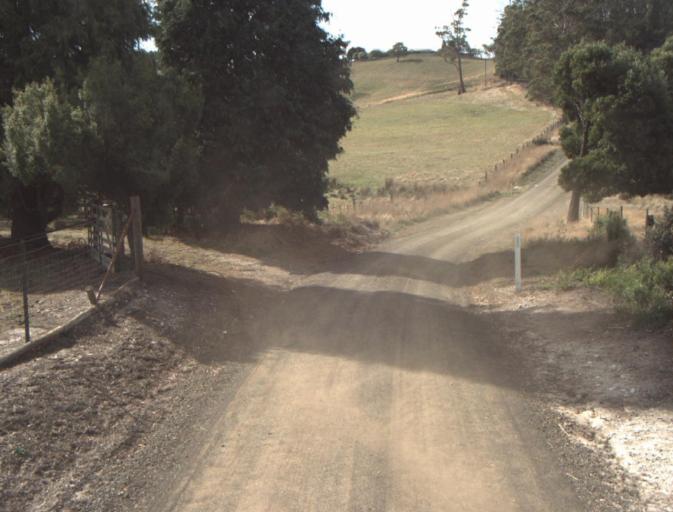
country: AU
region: Tasmania
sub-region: Launceston
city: Mayfield
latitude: -41.1884
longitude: 147.1907
